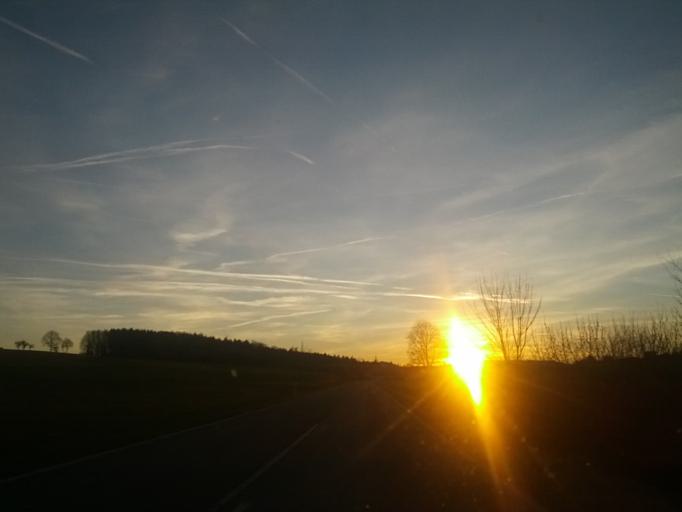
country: DE
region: Baden-Wuerttemberg
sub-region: Tuebingen Region
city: Rot an der Rot
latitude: 48.0061
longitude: 10.0181
